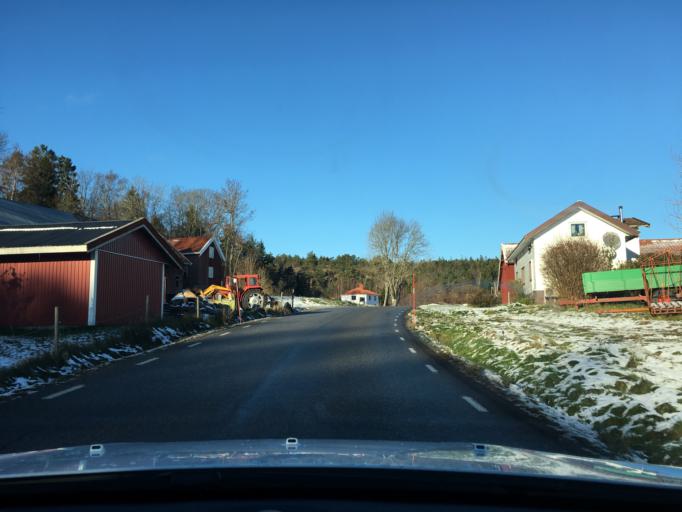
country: SE
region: Vaestra Goetaland
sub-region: Tjorns Kommun
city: Myggenas
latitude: 58.0407
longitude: 11.6737
